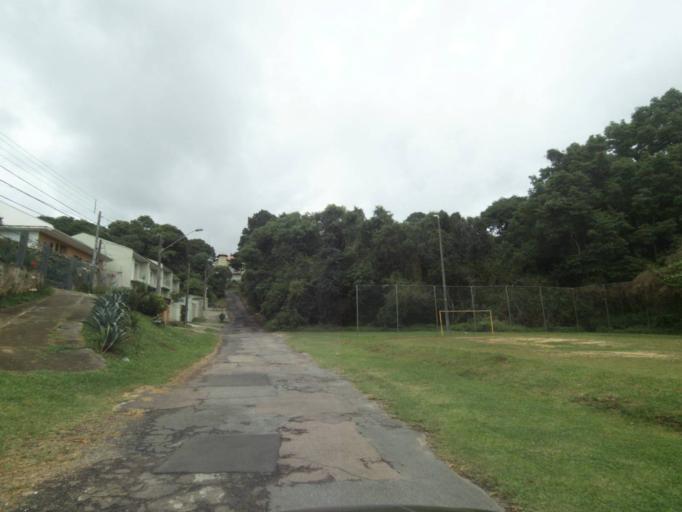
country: BR
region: Parana
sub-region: Curitiba
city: Curitiba
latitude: -25.4685
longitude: -49.3286
